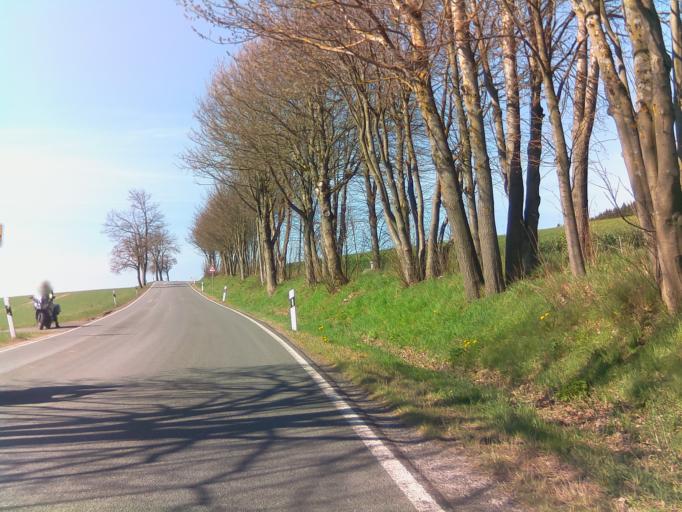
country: DE
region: Thuringia
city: Gillersdorf
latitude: 50.6043
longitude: 11.0130
